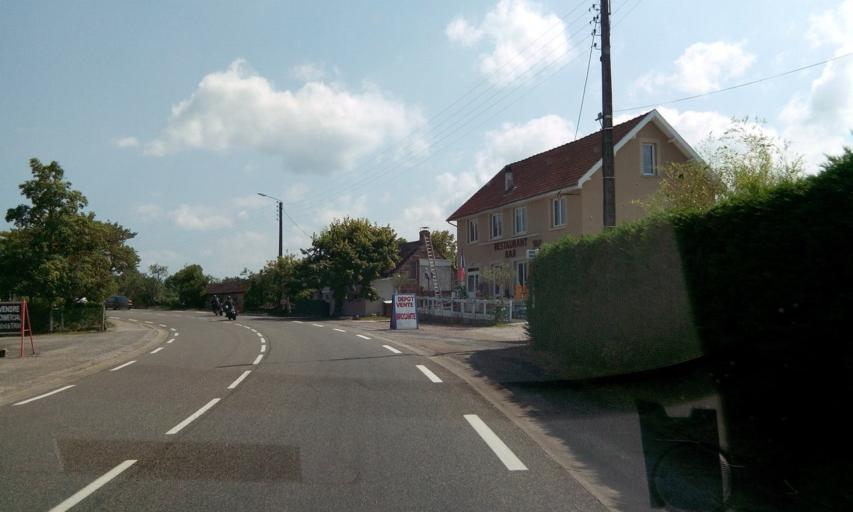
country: FR
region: Limousin
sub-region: Departement de la Correze
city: Cosnac
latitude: 45.1228
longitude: 1.5545
